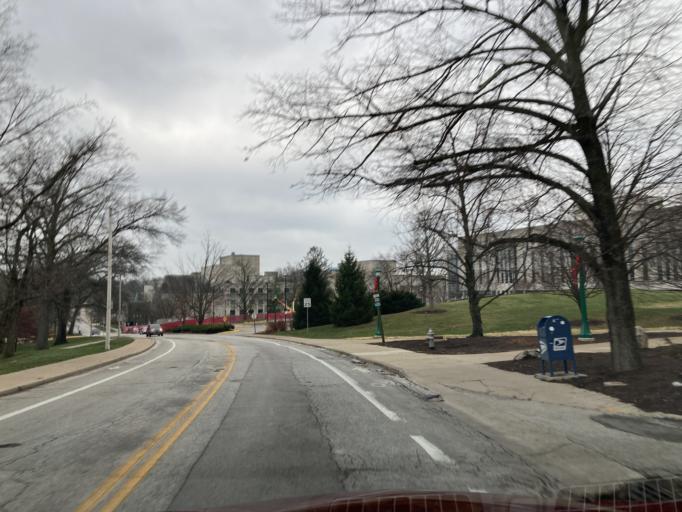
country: US
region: Indiana
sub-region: Monroe County
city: Bloomington
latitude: 39.1706
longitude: -86.5160
